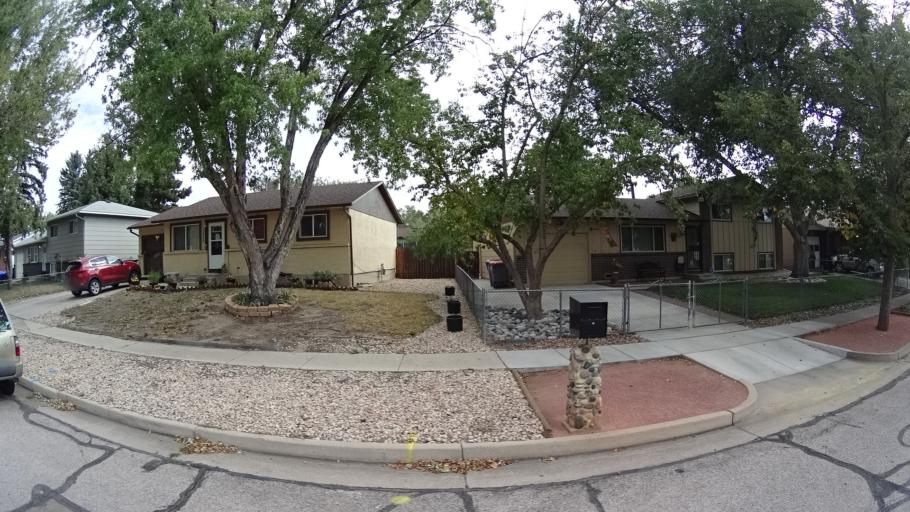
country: US
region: Colorado
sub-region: El Paso County
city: Cimarron Hills
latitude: 38.8554
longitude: -104.7516
